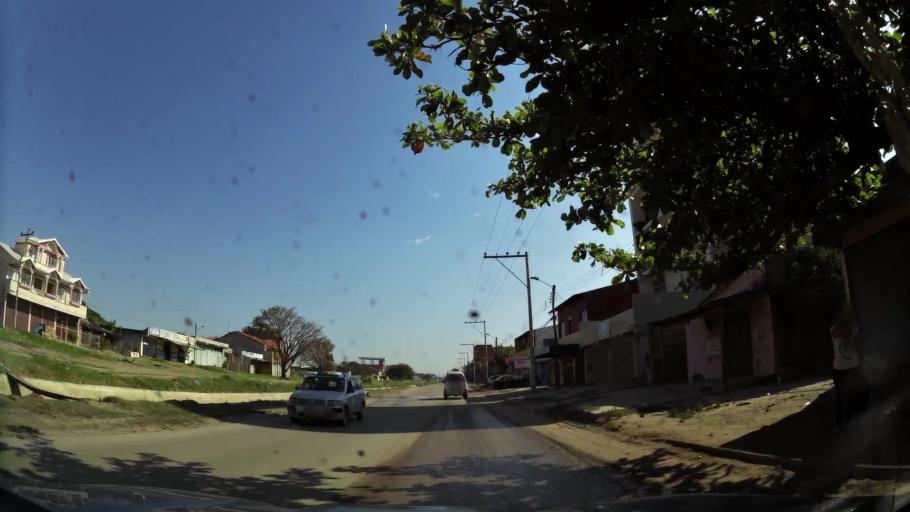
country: BO
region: Santa Cruz
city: Santa Cruz de la Sierra
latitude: -17.8201
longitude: -63.1223
